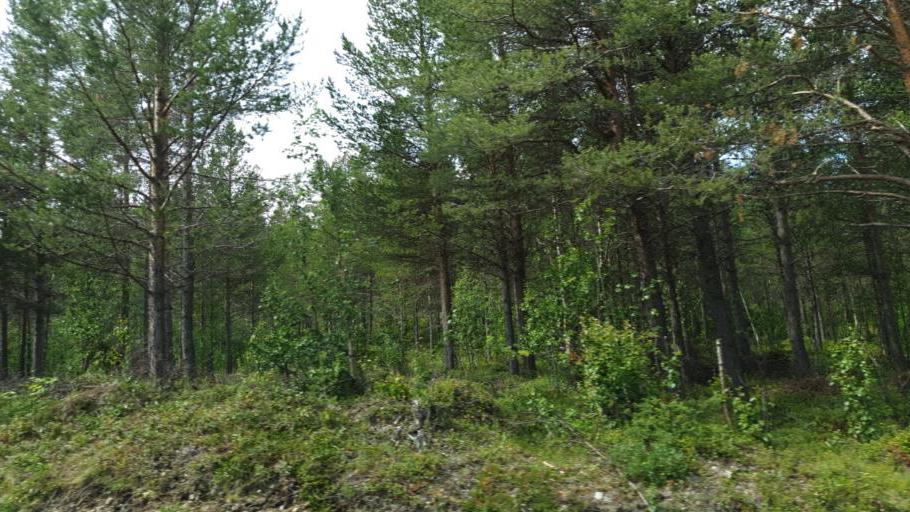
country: NO
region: Oppland
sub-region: Vaga
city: Vagamo
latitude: 61.7010
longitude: 9.0590
